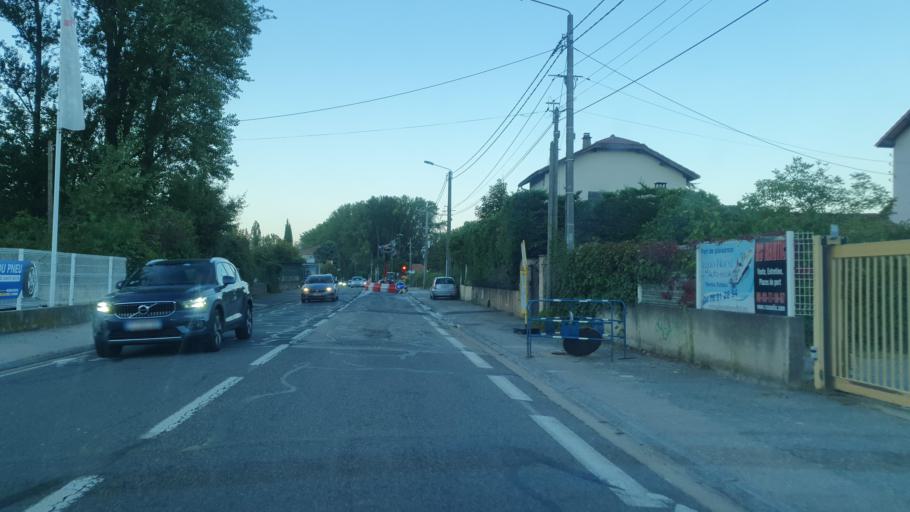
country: FR
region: Rhone-Alpes
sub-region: Departement du Rhone
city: Albigny-sur-Saone
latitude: 45.8554
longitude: 4.8345
